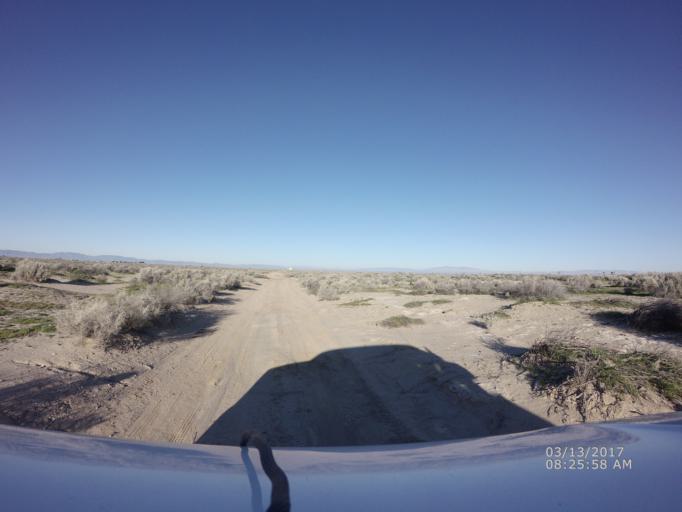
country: US
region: California
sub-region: Los Angeles County
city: Lake Los Angeles
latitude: 34.7343
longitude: -117.9337
